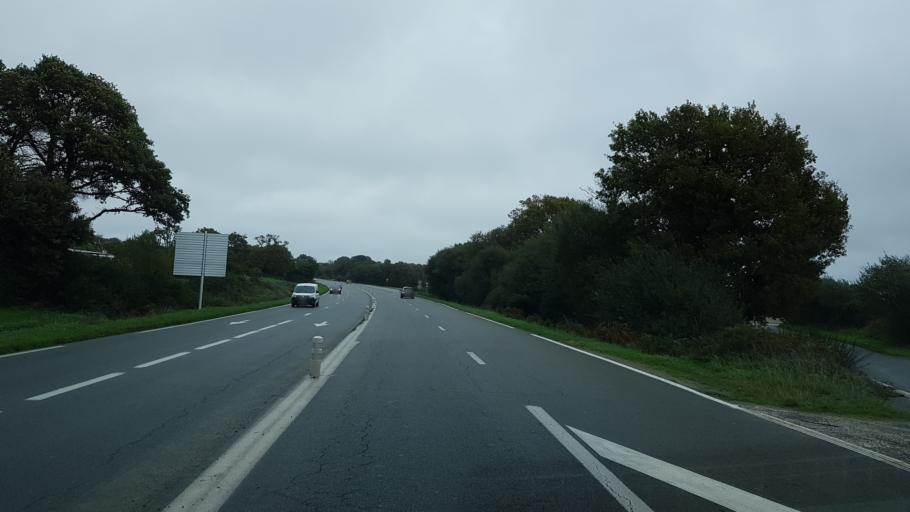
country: FR
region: Brittany
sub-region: Departement du Morbihan
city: Sarzeau
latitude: 47.5224
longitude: -2.7652
